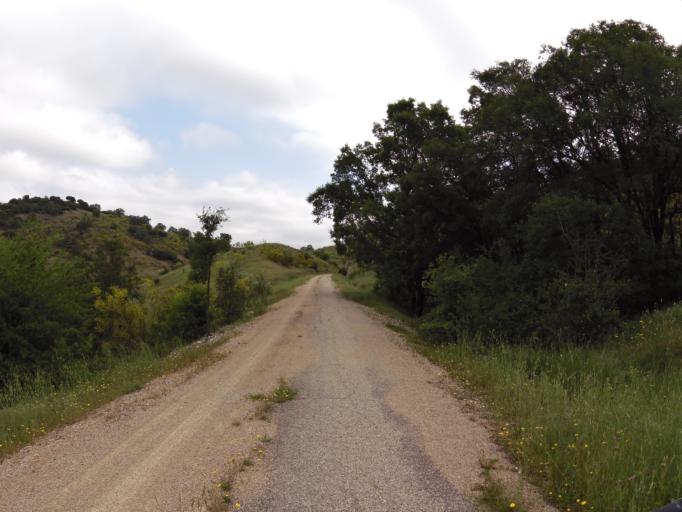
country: ES
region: Castille-La Mancha
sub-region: Provincia de Albacete
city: Alcaraz
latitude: 38.7084
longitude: -2.4995
